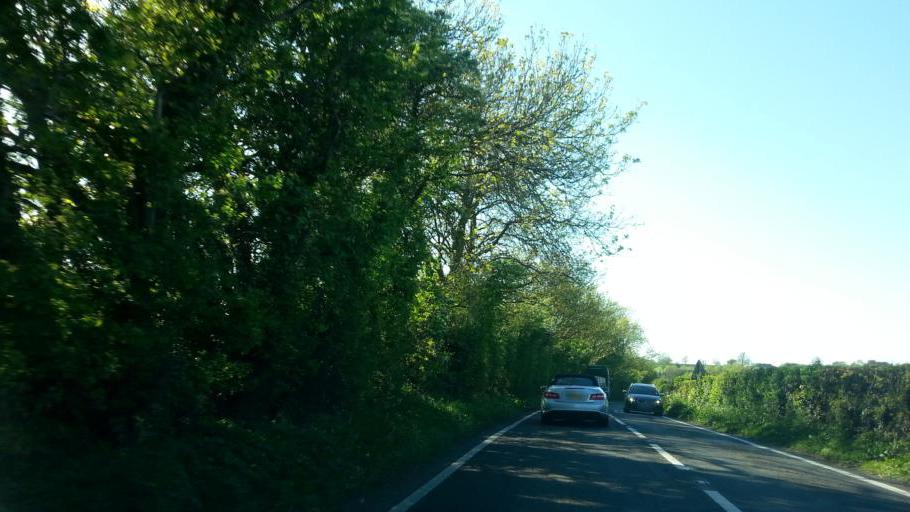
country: GB
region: England
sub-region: Somerset
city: Shepton Mallet
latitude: 51.1659
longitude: -2.5311
